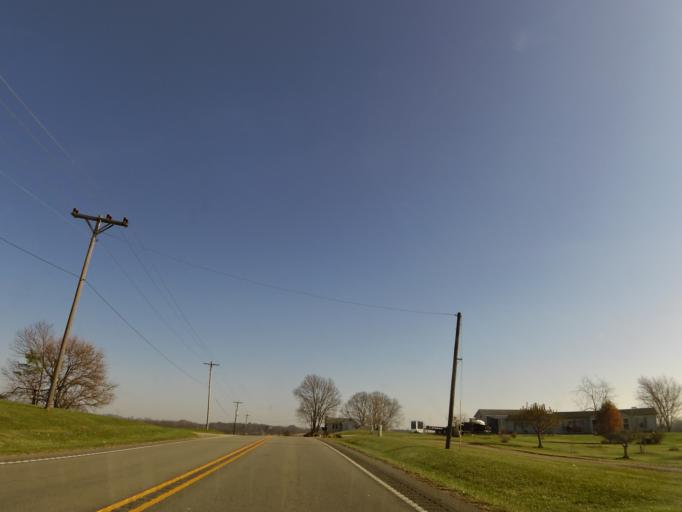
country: US
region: Indiana
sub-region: Fayette County
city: Connersville
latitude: 39.6386
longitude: -85.0841
